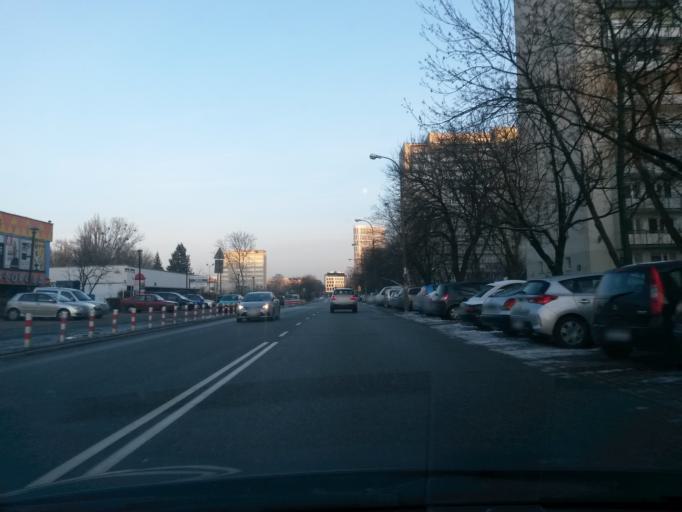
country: PL
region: Masovian Voivodeship
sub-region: Warszawa
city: Warsaw
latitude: 52.2111
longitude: 21.0100
